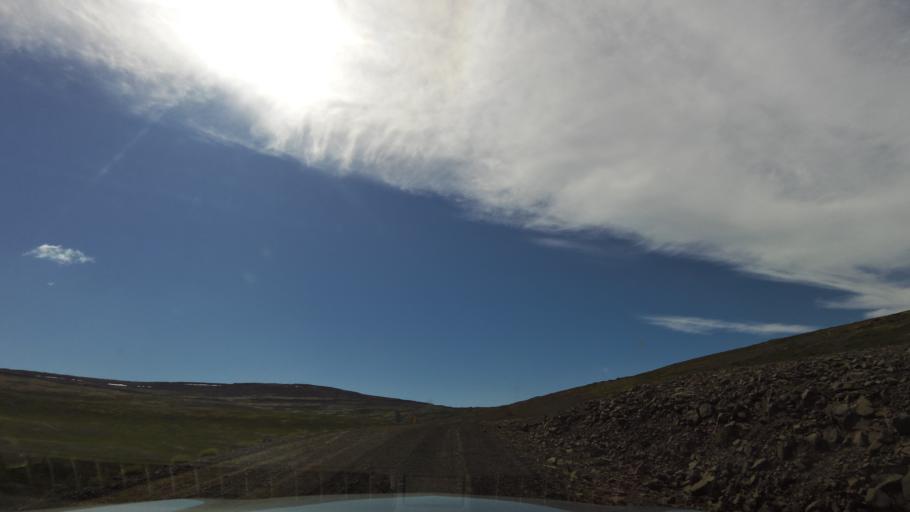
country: IS
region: West
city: Olafsvik
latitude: 65.5219
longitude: -23.9267
